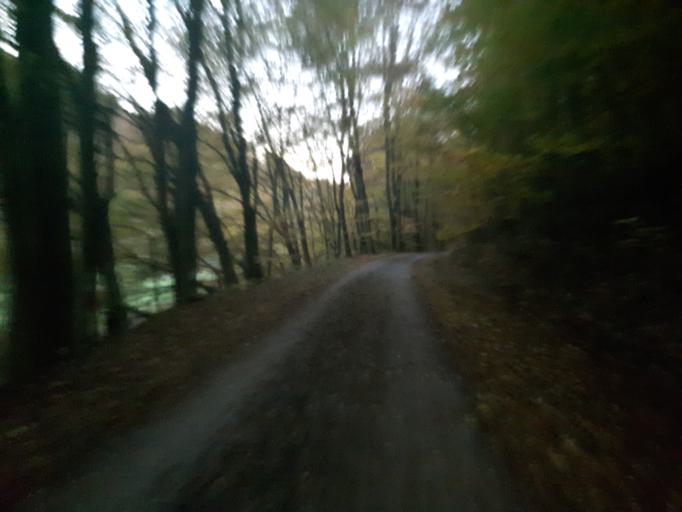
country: DE
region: Bavaria
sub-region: Regierungsbezirk Unterfranken
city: Leidersbach
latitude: 49.8944
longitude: 9.2567
